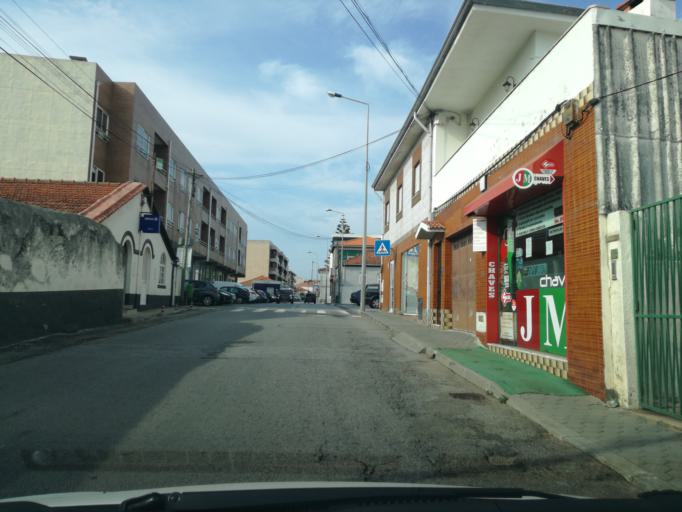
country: PT
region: Porto
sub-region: Vila Nova de Gaia
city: Sao Felix da Marinha
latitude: 41.0464
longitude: -8.6285
